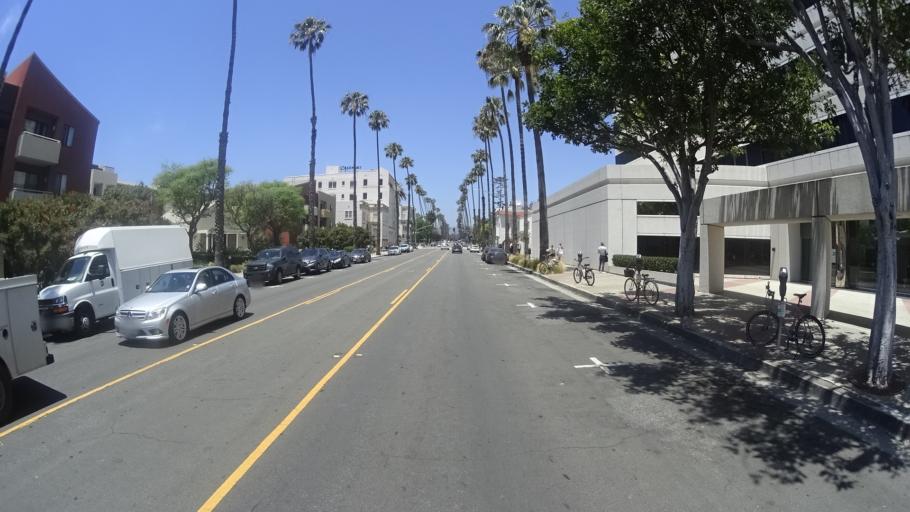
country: US
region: California
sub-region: Los Angeles County
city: Santa Monica
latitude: 34.0196
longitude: -118.4988
